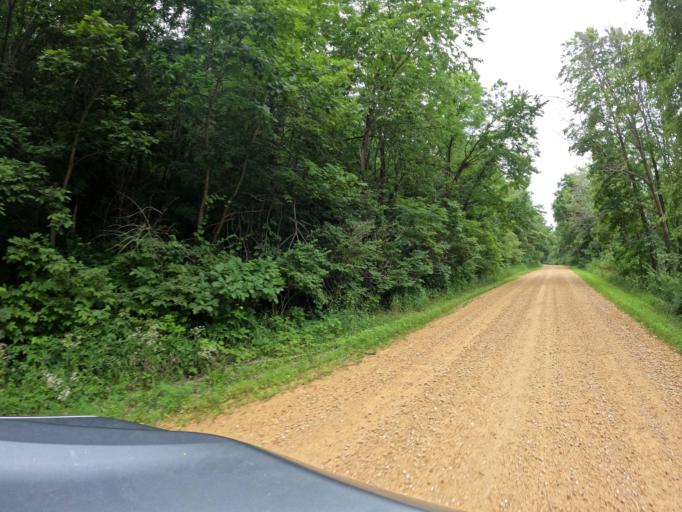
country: US
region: Illinois
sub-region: Carroll County
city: Savanna
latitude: 41.9860
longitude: -90.1727
